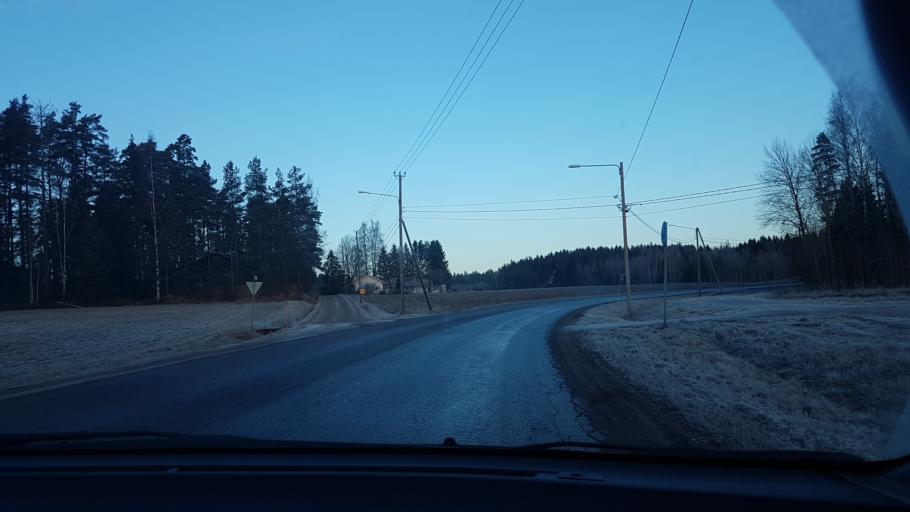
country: FI
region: Uusimaa
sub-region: Helsinki
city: Tuusula
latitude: 60.3720
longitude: 24.9701
